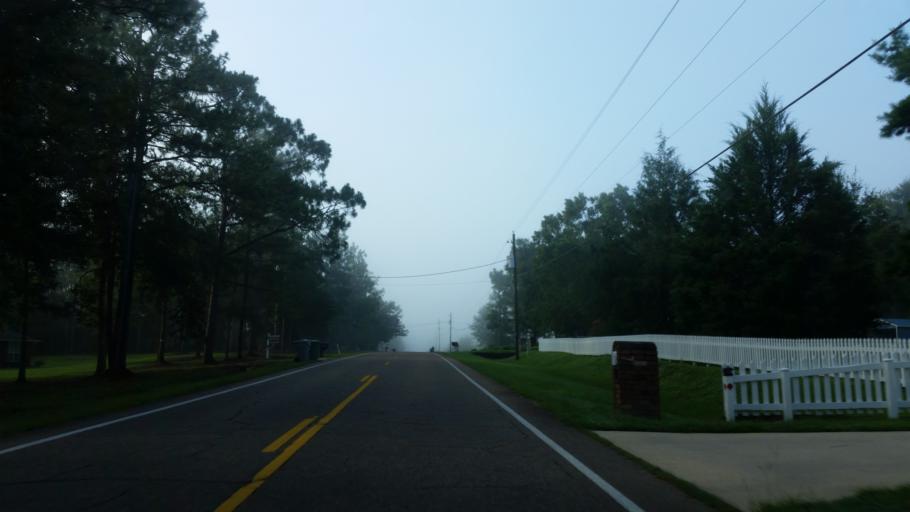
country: US
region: Florida
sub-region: Escambia County
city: Molino
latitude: 30.7316
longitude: -87.3449
